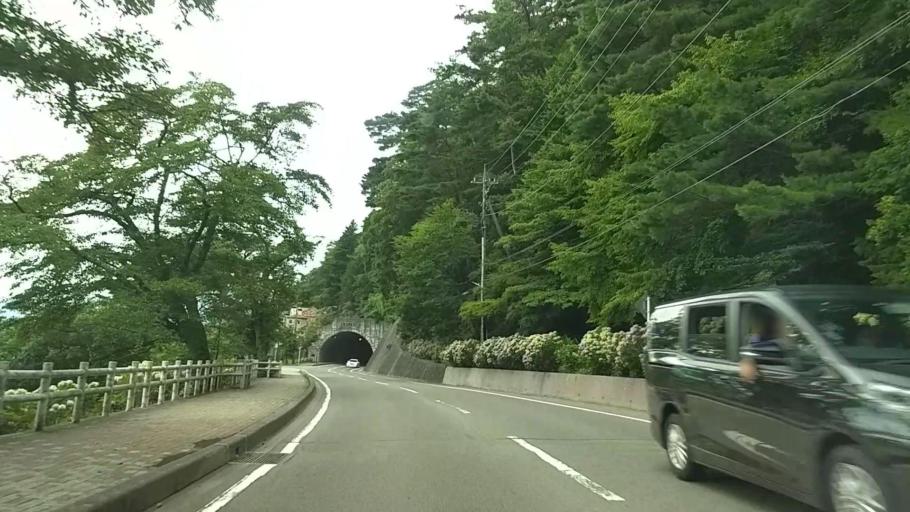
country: JP
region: Yamanashi
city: Fujikawaguchiko
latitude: 35.5244
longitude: 138.7580
